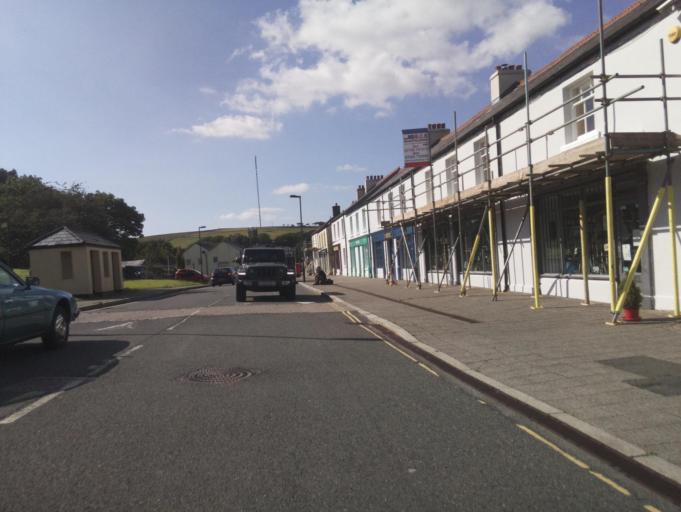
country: GB
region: England
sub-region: Devon
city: Yelverton
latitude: 50.5442
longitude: -3.9908
